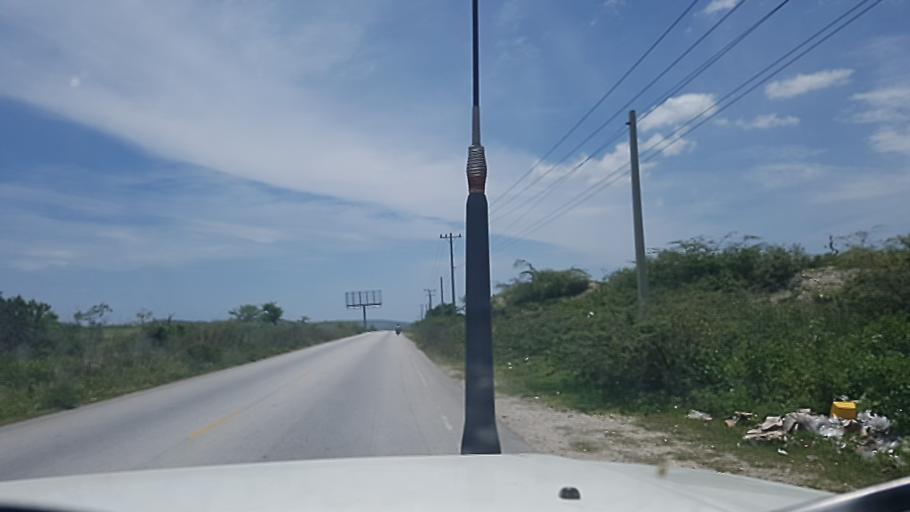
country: HT
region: Artibonite
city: Saint-Marc
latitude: 19.1519
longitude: -72.6317
